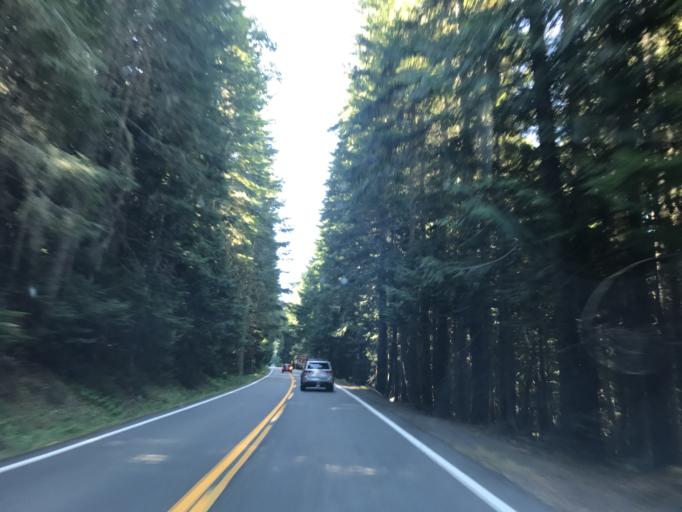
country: US
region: Washington
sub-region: King County
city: Enumclaw
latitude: 46.9199
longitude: -121.5347
